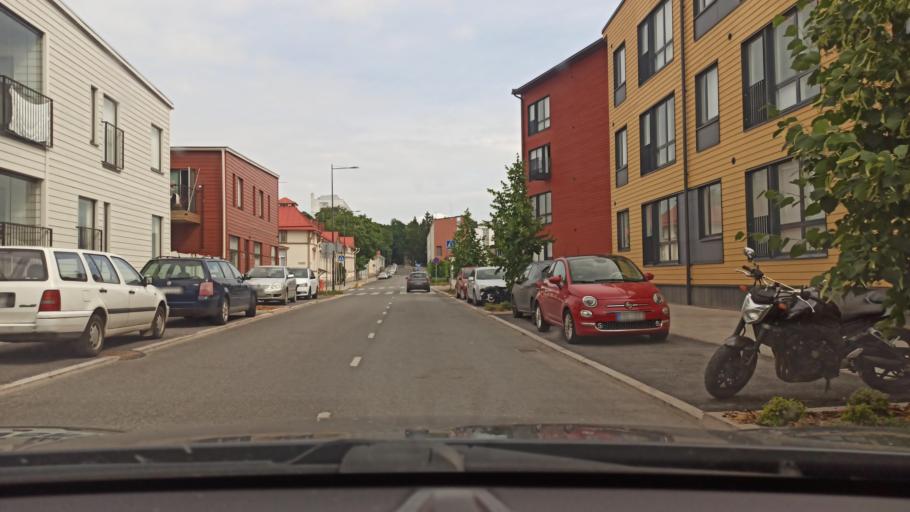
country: FI
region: Varsinais-Suomi
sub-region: Turku
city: Turku
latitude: 60.4389
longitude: 22.2340
